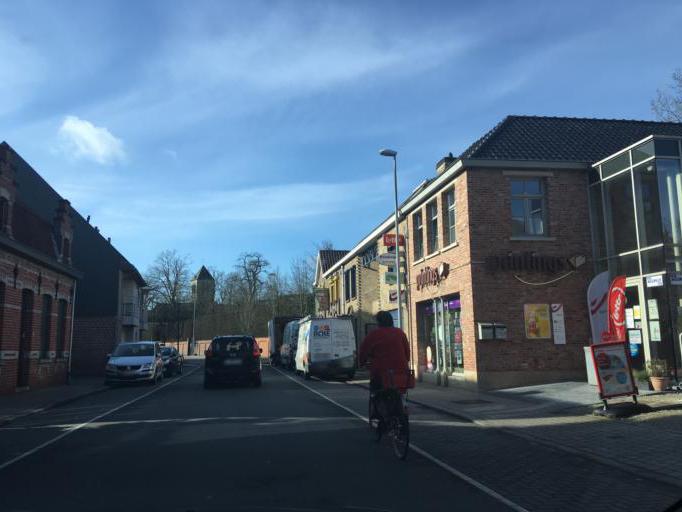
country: BE
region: Flanders
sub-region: Provincie West-Vlaanderen
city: Wevelgem
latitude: 50.8427
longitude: 3.1643
